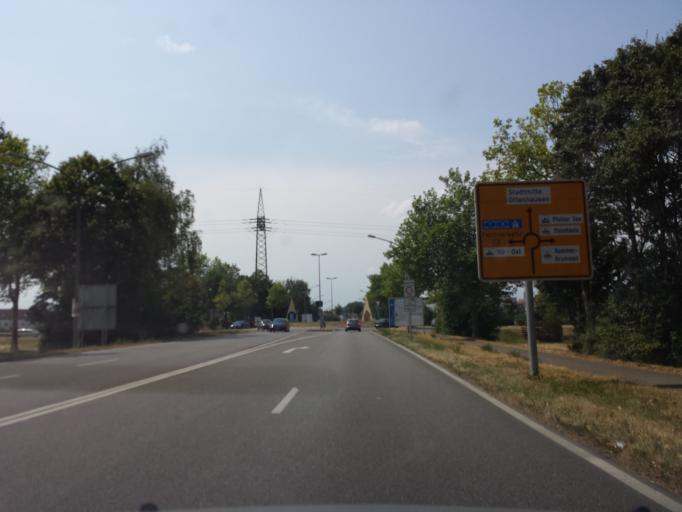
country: DE
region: Bavaria
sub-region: Swabia
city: Neu-Ulm
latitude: 48.4034
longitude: 10.0299
